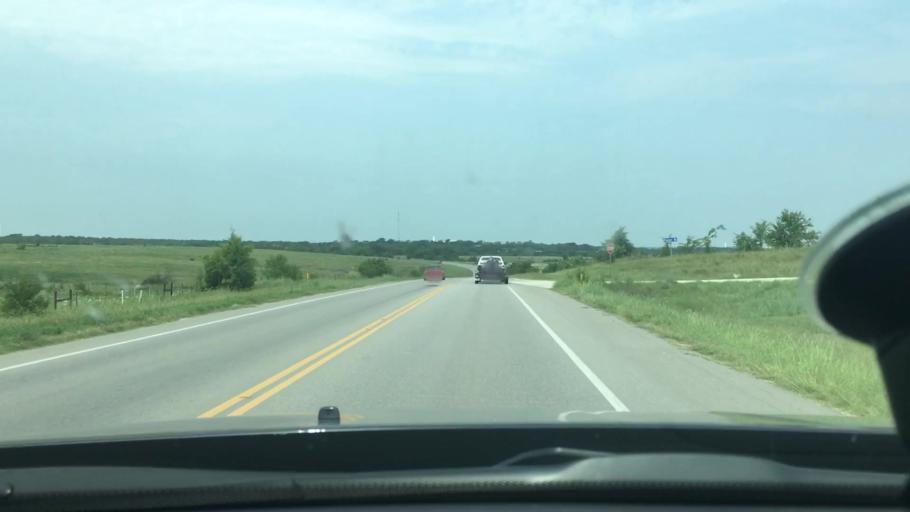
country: US
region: Oklahoma
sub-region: Marshall County
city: Madill
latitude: 34.0559
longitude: -96.7476
